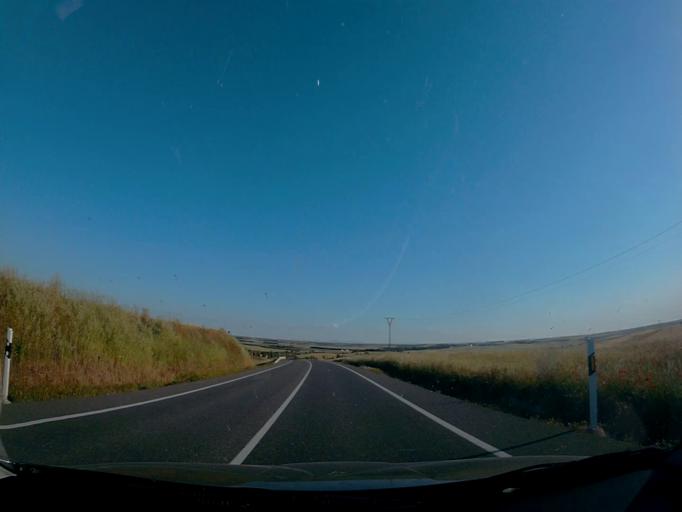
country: ES
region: Castille-La Mancha
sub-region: Province of Toledo
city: Maqueda
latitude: 40.0695
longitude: -4.3779
